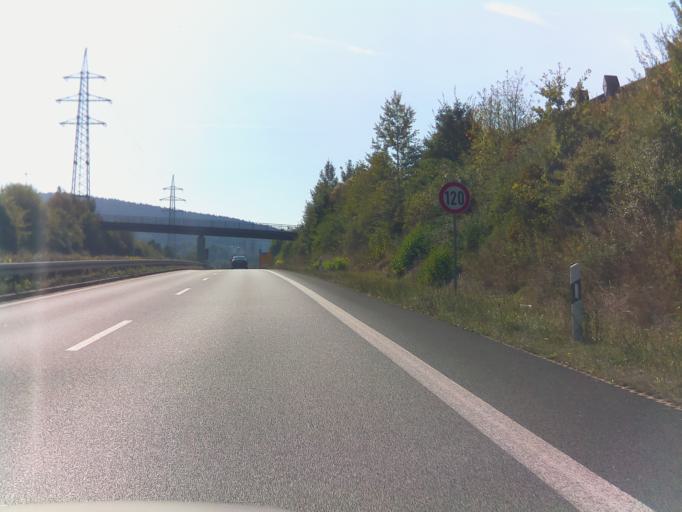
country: DE
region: Bavaria
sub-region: Upper Franconia
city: Lichtenfels
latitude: 50.1459
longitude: 11.0796
